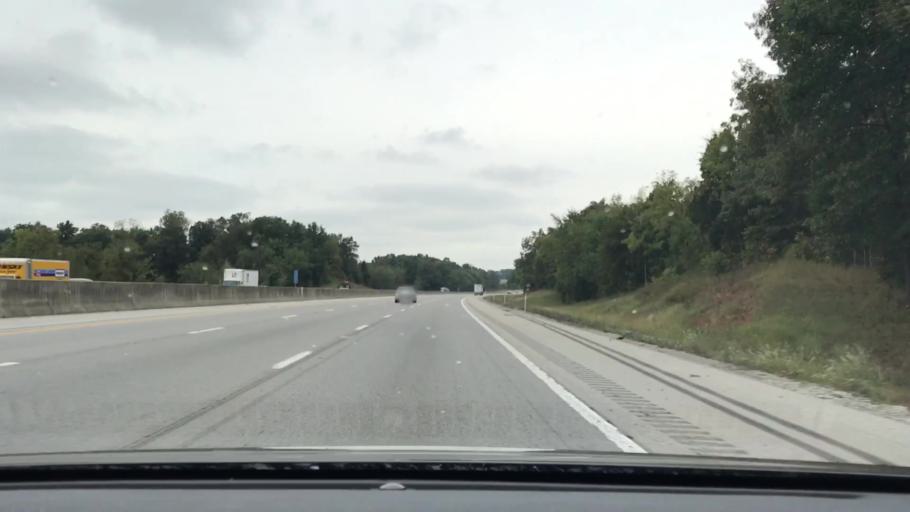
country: US
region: Kentucky
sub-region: Simpson County
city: Franklin
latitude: 36.7541
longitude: -86.4898
